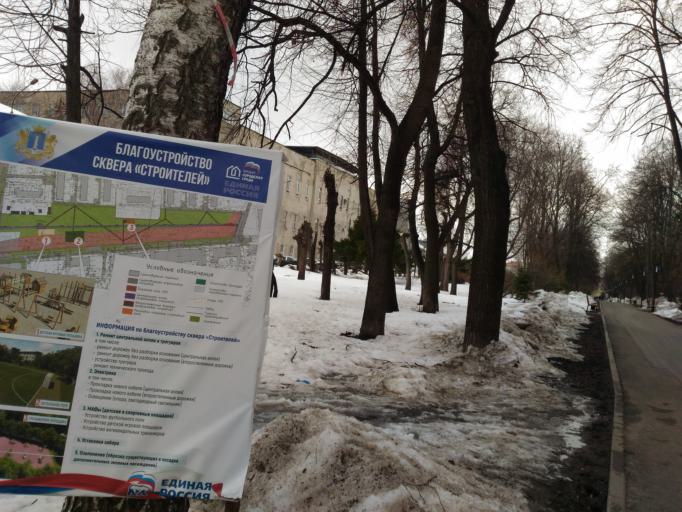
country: RU
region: Ulyanovsk
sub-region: Ulyanovskiy Rayon
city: Ulyanovsk
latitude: 54.3057
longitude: 48.3858
